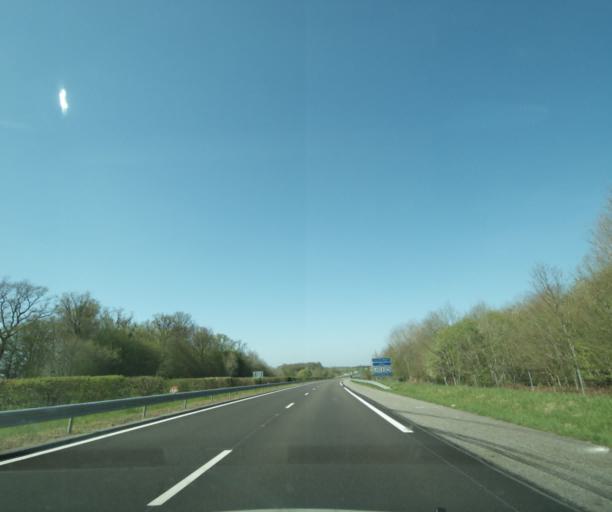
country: FR
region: Bourgogne
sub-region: Departement de la Nievre
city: Neuvy-sur-Loire
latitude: 47.5040
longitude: 2.9231
